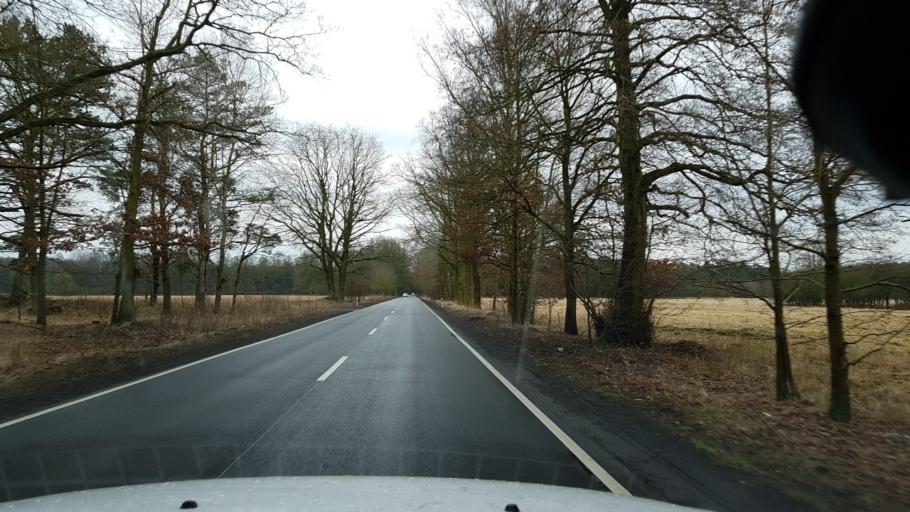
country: PL
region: West Pomeranian Voivodeship
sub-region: Powiat goleniowski
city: Stepnica
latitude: 53.6463
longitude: 14.6554
